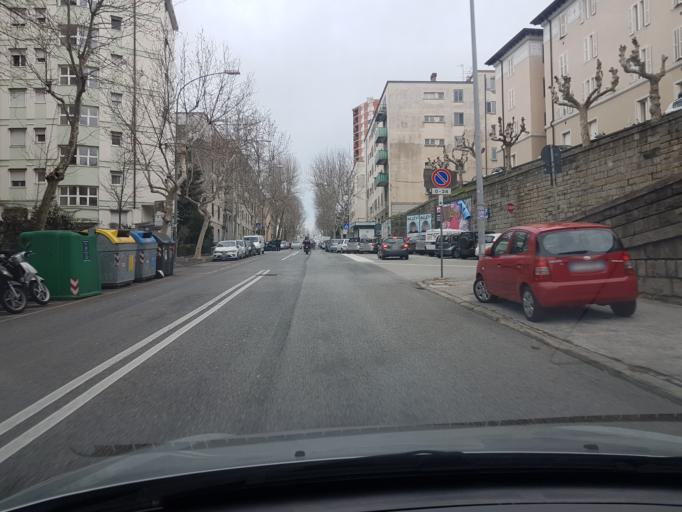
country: IT
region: Friuli Venezia Giulia
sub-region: Provincia di Trieste
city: Trieste
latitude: 45.6390
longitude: 13.7692
